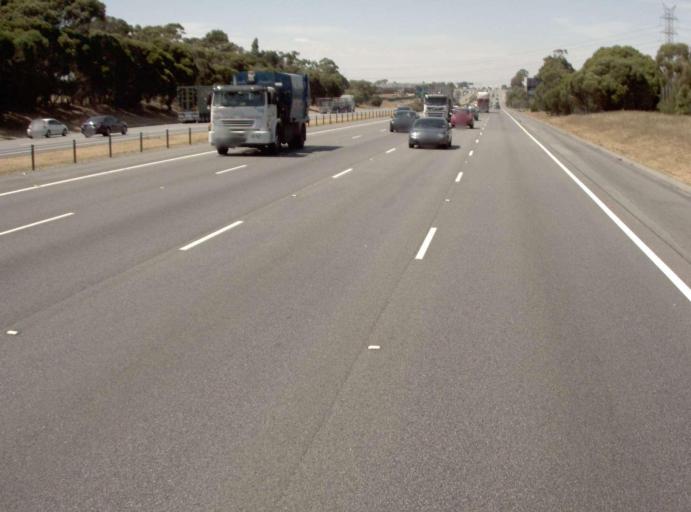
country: AU
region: Victoria
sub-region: Monash
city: Mulgrave
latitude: -37.9266
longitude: 145.1812
